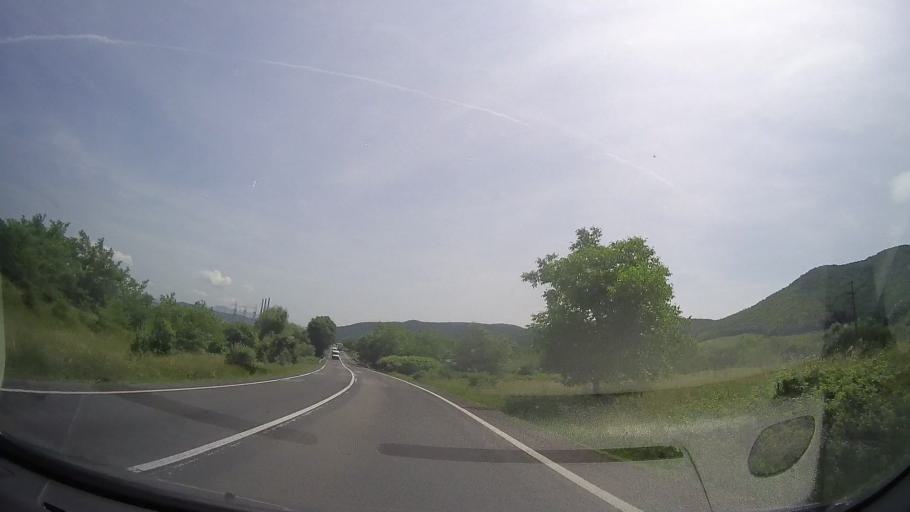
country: RO
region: Hunedoara
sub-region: Comuna Branisca
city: Branisca
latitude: 45.9036
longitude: 22.7888
